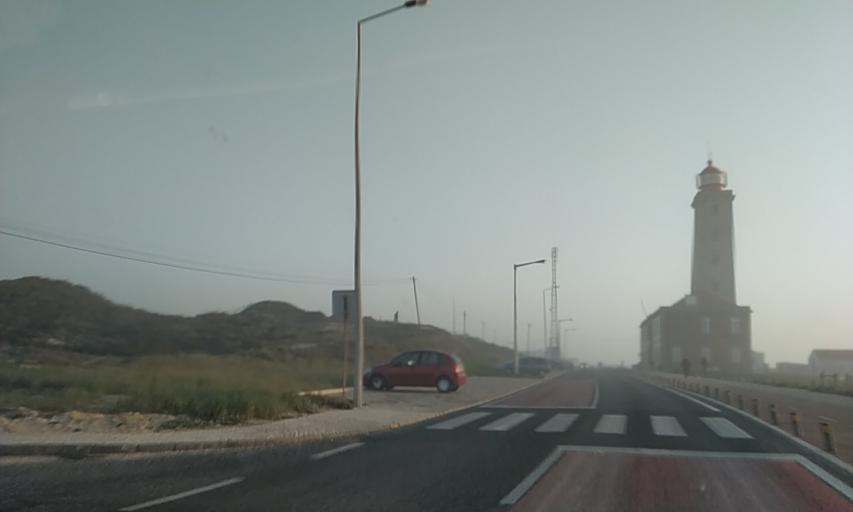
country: PT
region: Leiria
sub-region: Marinha Grande
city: Marinha Grande
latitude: 39.7650
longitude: -9.0305
